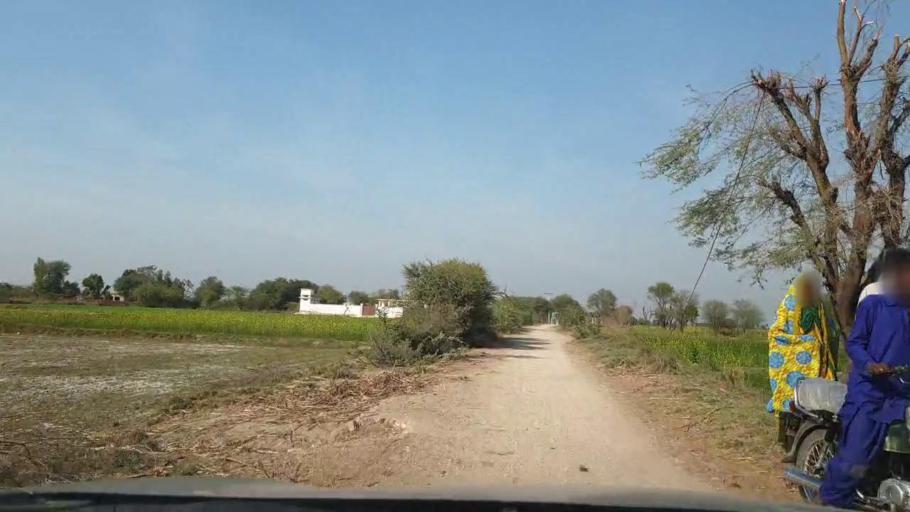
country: PK
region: Sindh
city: Berani
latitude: 25.7237
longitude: 68.7615
